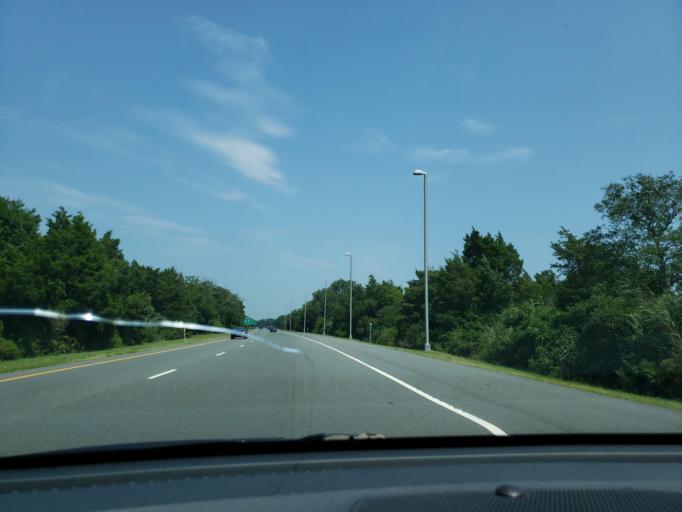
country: US
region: New Jersey
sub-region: Cape May County
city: Sea Isle City
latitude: 39.1968
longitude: -74.7058
